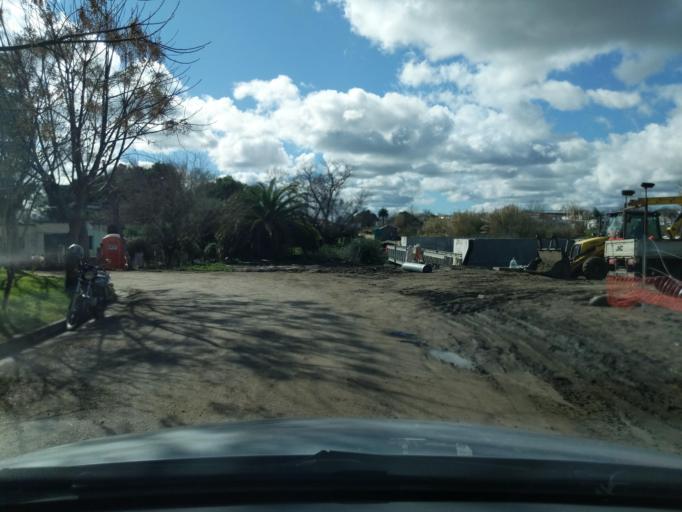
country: UY
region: Florida
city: Florida
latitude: -34.0931
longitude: -56.2249
